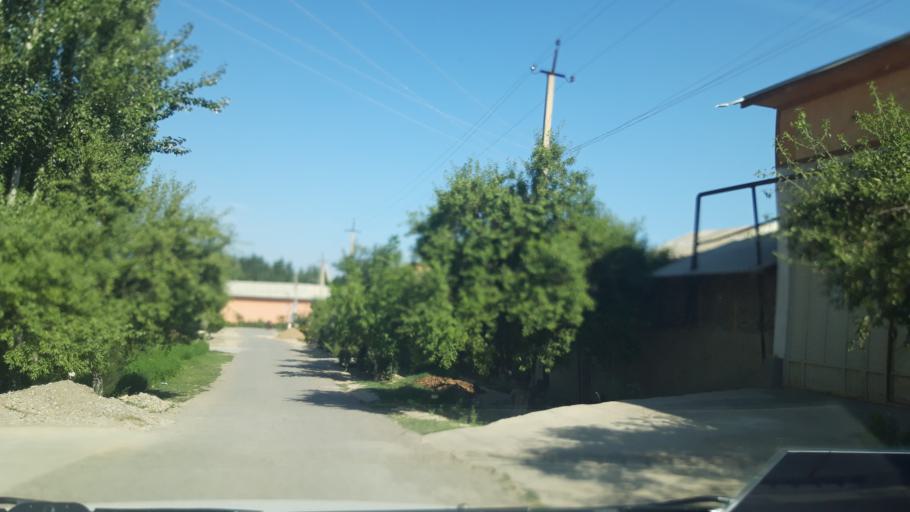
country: UZ
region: Namangan
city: Yangiqo`rg`on
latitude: 41.2023
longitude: 71.7241
